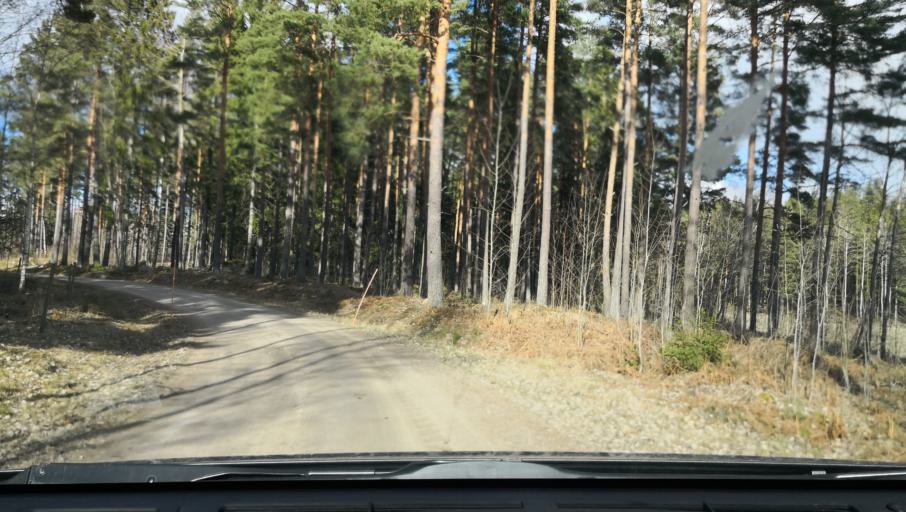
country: SE
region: OErebro
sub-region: Lindesbergs Kommun
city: Fellingsbro
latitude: 59.4280
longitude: 15.6868
